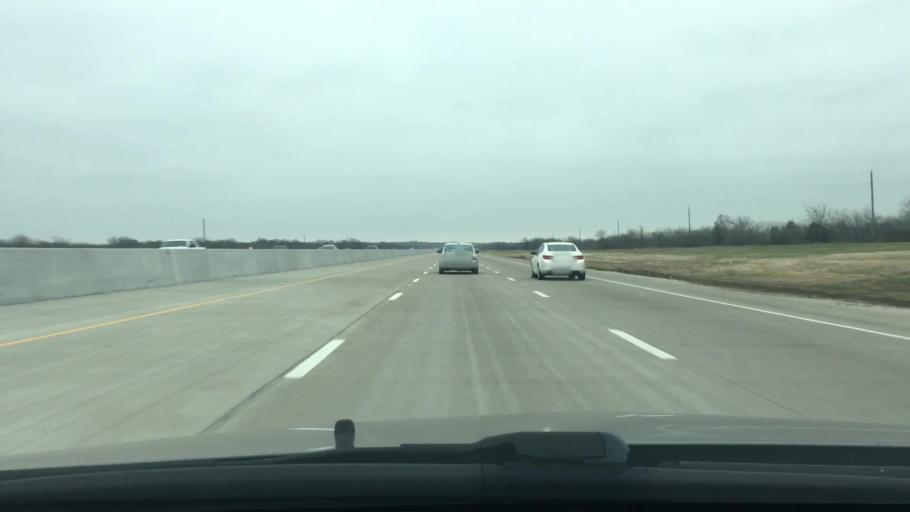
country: US
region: Texas
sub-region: Freestone County
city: Wortham
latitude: 31.9028
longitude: -96.3799
